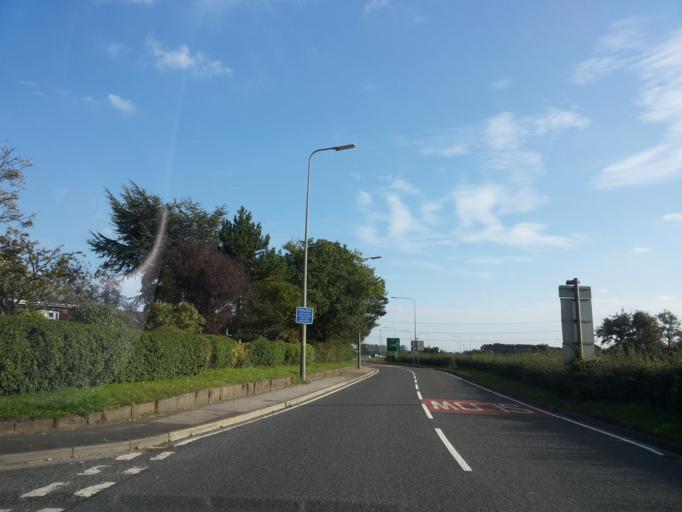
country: GB
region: England
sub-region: North Yorkshire
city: Camblesforth
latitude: 53.7240
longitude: -1.0213
